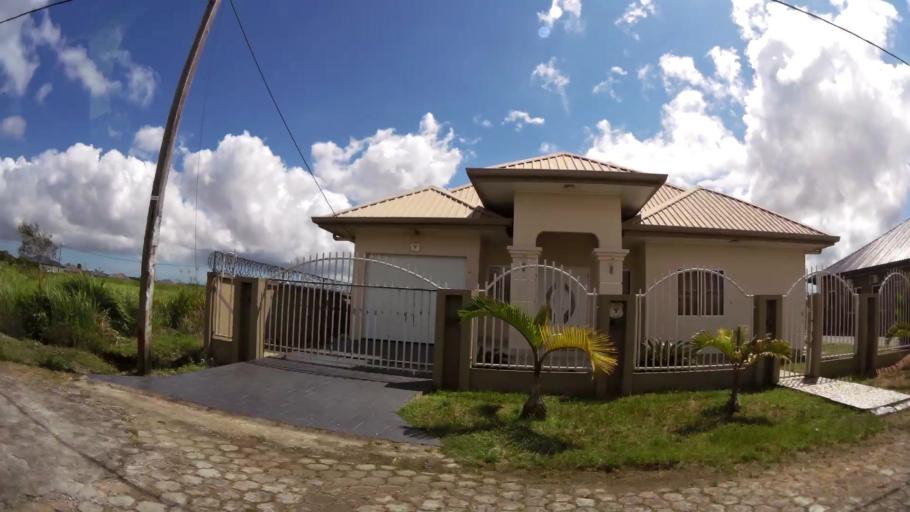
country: SR
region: Paramaribo
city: Paramaribo
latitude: 5.8716
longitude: -55.1315
